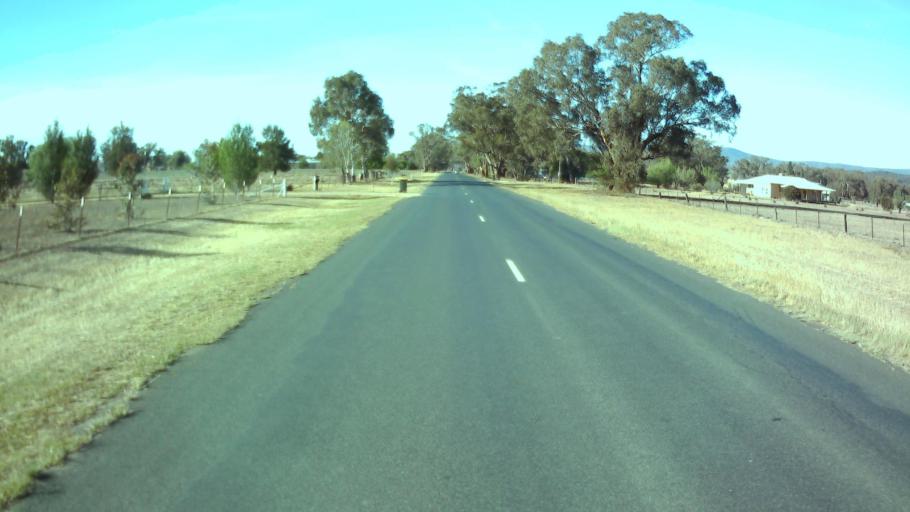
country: AU
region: New South Wales
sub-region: Weddin
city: Grenfell
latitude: -33.9110
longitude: 148.1446
